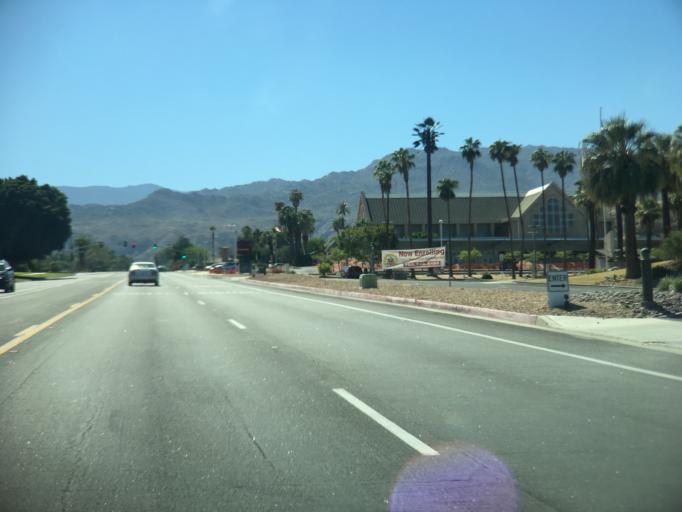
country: US
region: California
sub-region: Riverside County
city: Palm Desert
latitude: 33.7056
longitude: -116.3963
